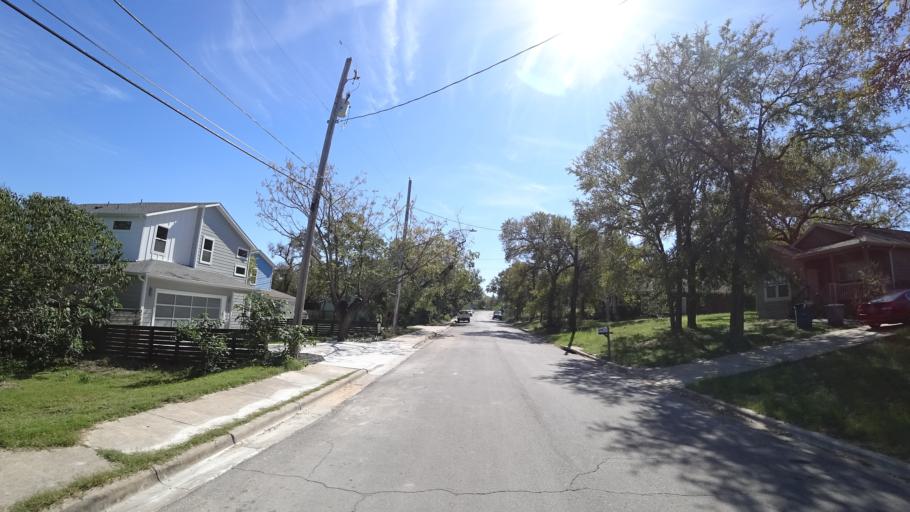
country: US
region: Texas
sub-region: Travis County
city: Austin
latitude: 30.2723
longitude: -97.6814
